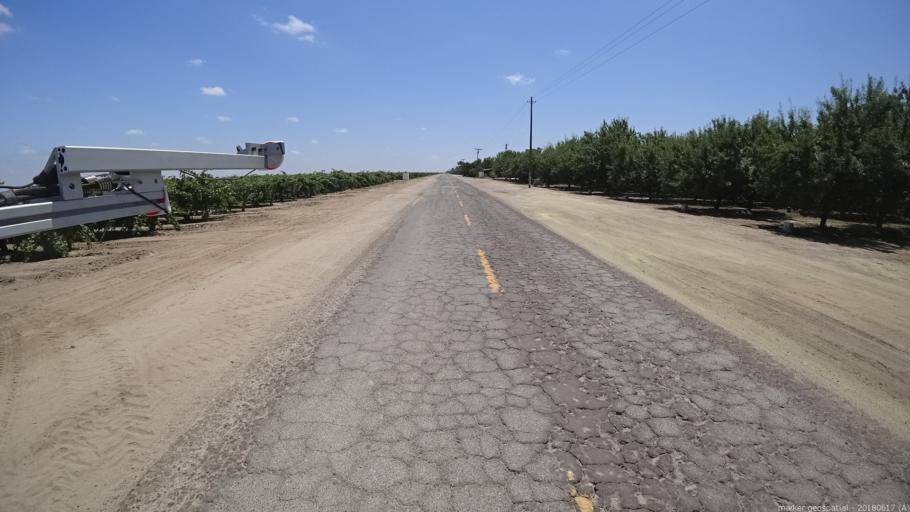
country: US
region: California
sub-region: Fresno County
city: Biola
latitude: 36.8305
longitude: -120.1510
